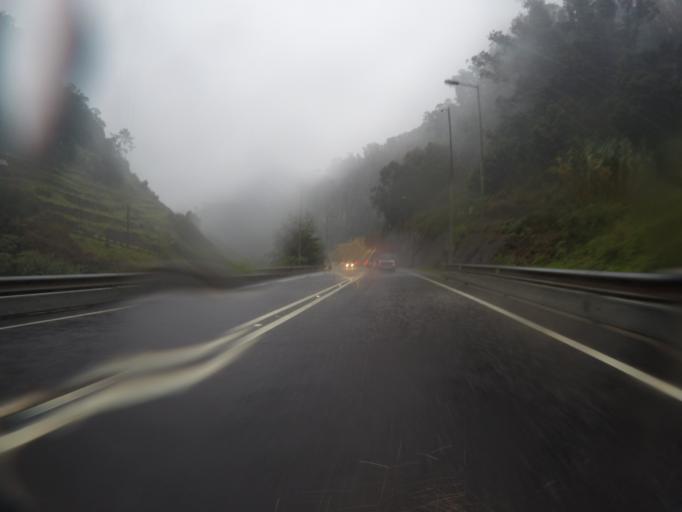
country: PT
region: Madeira
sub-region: Santa Cruz
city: Santa Cruz
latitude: 32.7355
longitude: -16.8077
